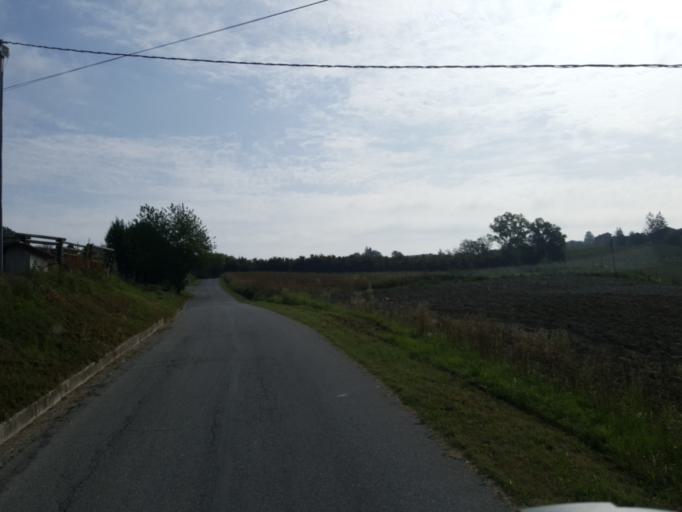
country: IT
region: Piedmont
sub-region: Provincia di Cuneo
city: Novello
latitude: 44.5948
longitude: 7.9031
